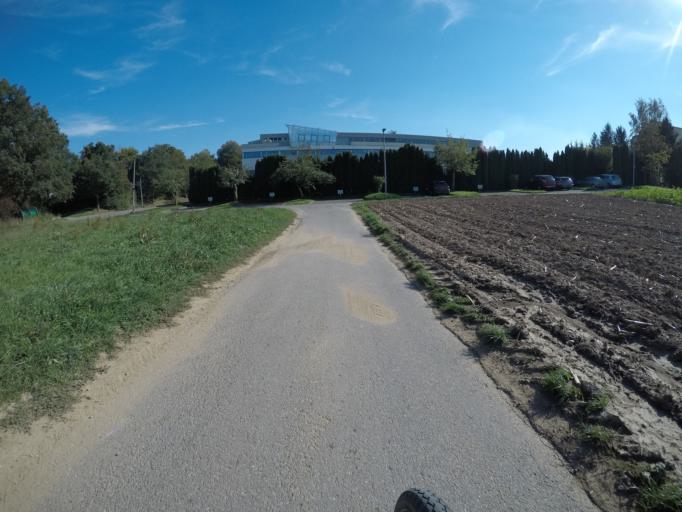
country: DE
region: Baden-Wuerttemberg
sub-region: Regierungsbezirk Stuttgart
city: Steinenbronn
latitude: 48.6948
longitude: 9.1300
